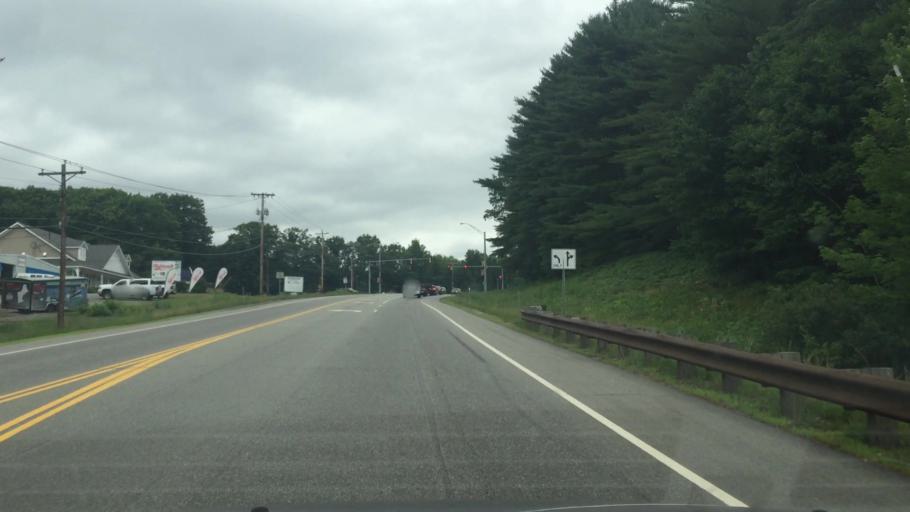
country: US
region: New Hampshire
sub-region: Belknap County
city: Meredith
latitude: 43.6375
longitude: -71.5301
